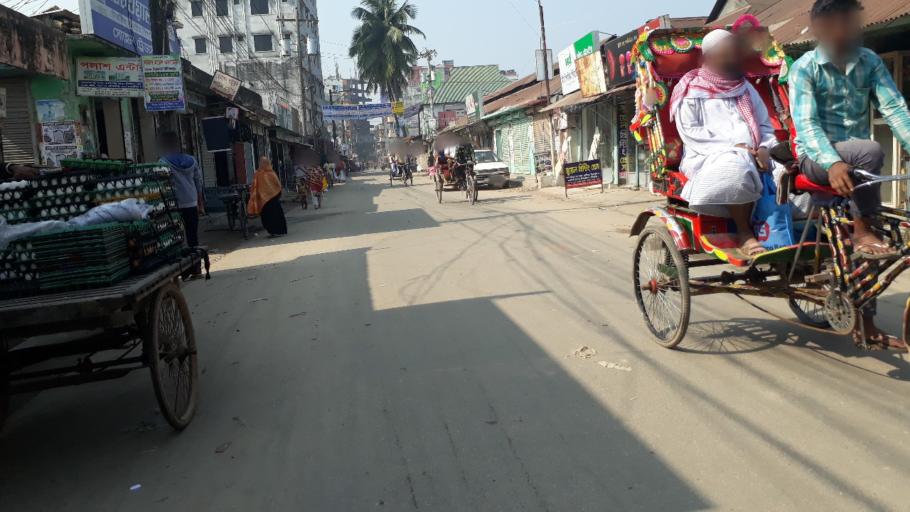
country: BD
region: Dhaka
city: Tungi
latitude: 23.8467
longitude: 90.2501
